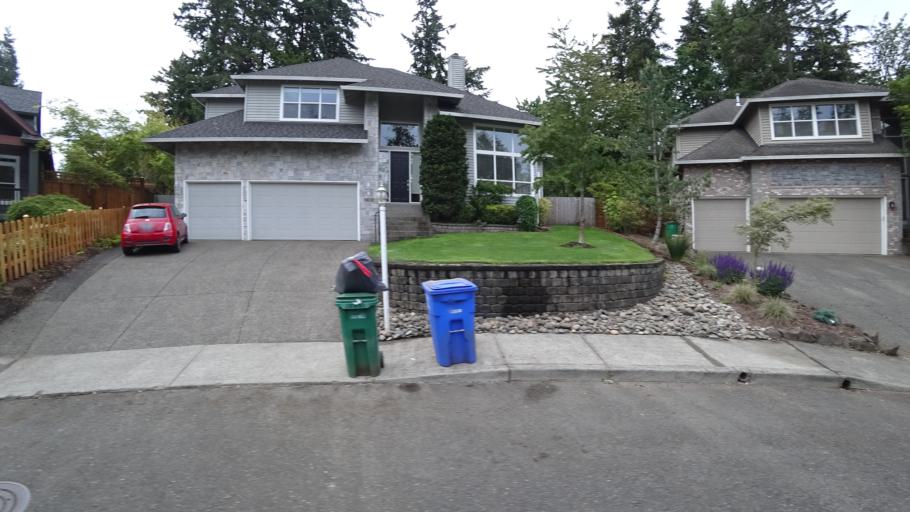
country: US
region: Oregon
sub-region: Washington County
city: Garden Home-Whitford
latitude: 45.4686
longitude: -122.7416
